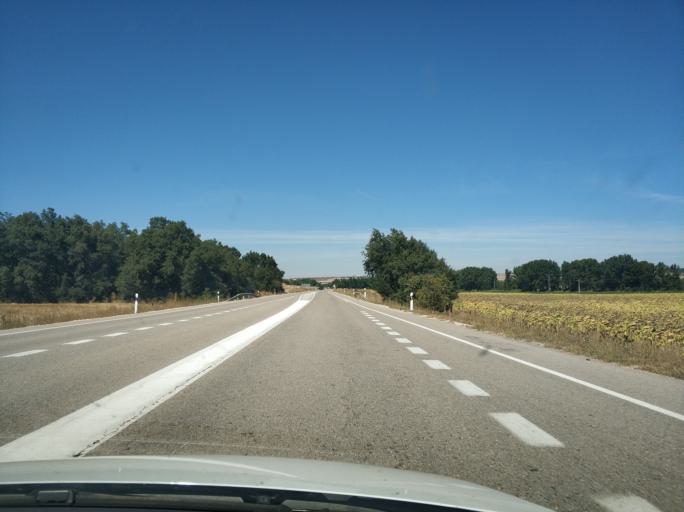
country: ES
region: Castille and Leon
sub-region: Provincia de Burgos
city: Sarracin
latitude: 42.2443
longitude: -3.6774
